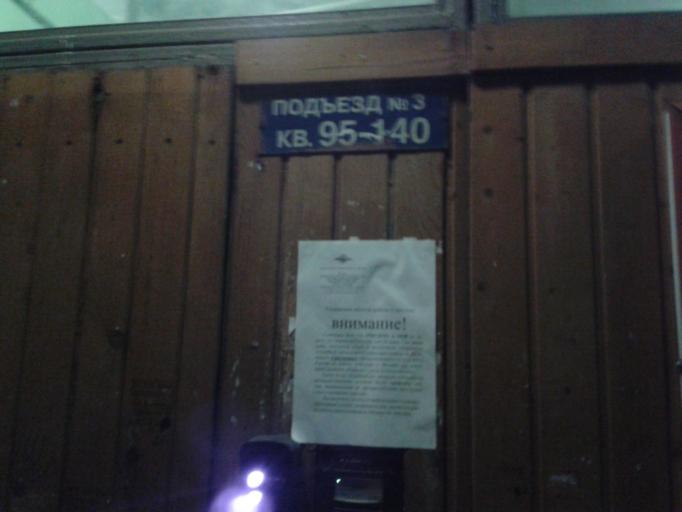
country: RU
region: Moscow
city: Strogino
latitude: 55.8081
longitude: 37.4057
